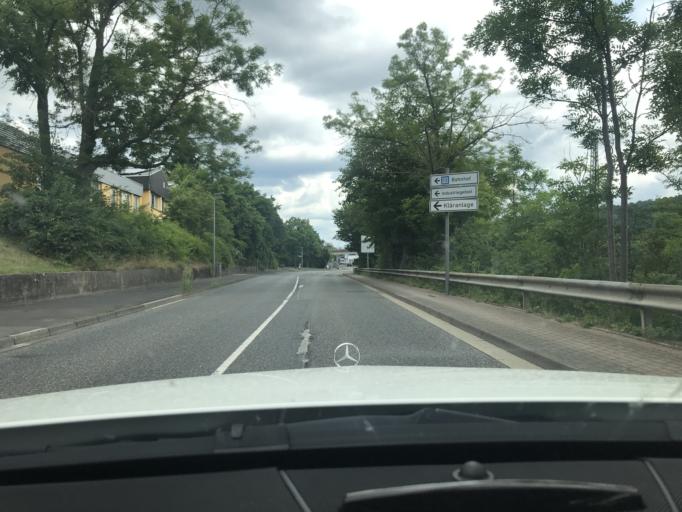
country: DE
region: Hesse
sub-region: Regierungsbezirk Kassel
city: Bad Hersfeld
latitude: 50.8722
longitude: 9.7171
